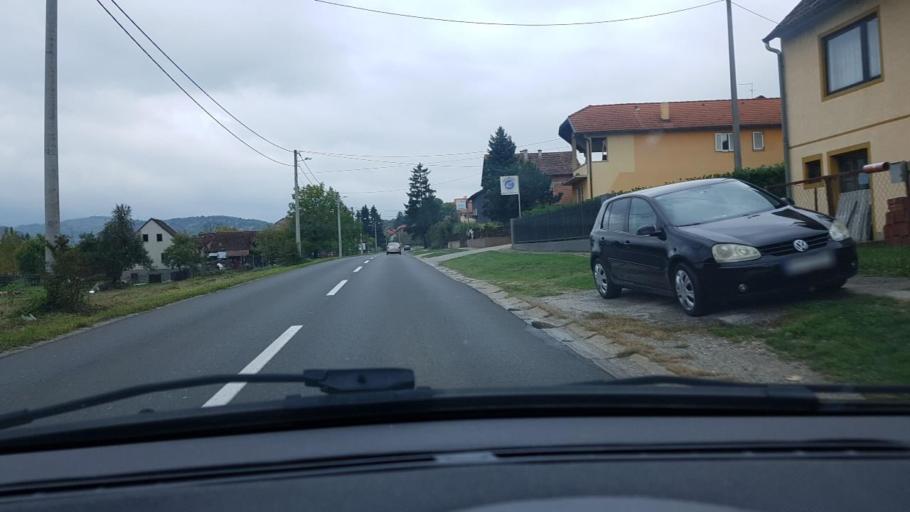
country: HR
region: Grad Zagreb
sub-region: Sesvete
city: Sesvete
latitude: 45.8649
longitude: 16.1151
